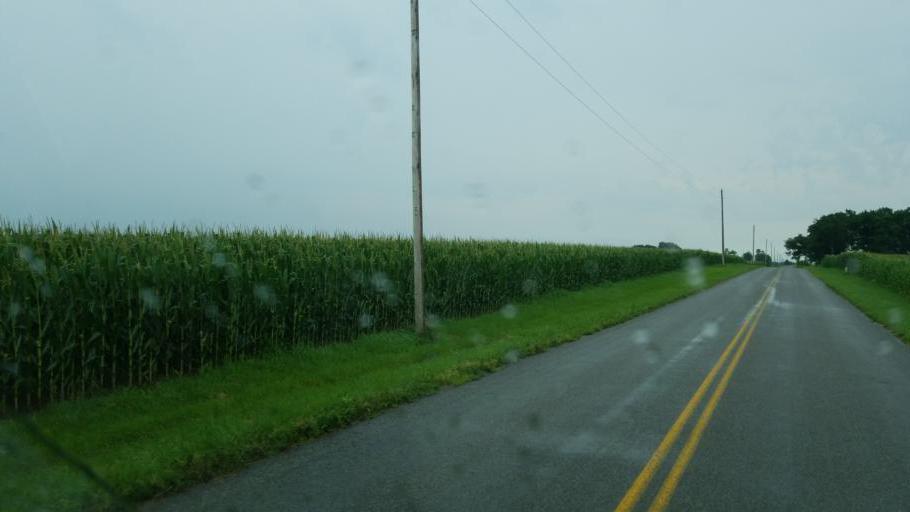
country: US
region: Ohio
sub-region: Union County
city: Richwood
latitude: 40.5282
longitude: -83.4348
